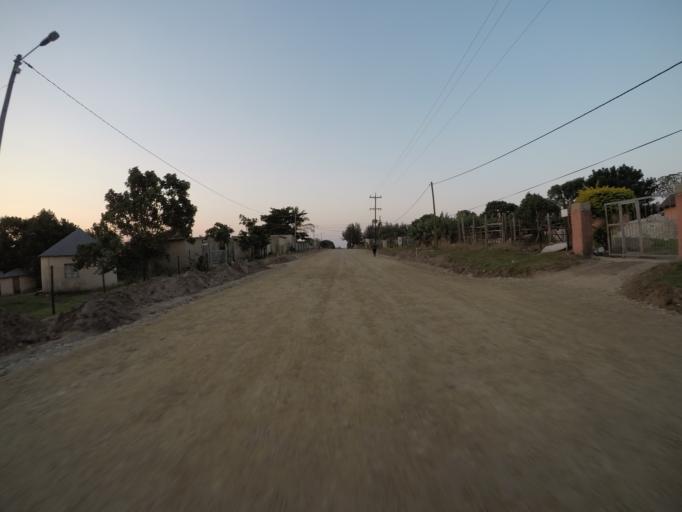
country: ZA
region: KwaZulu-Natal
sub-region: uThungulu District Municipality
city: Richards Bay
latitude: -28.7576
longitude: 32.1290
